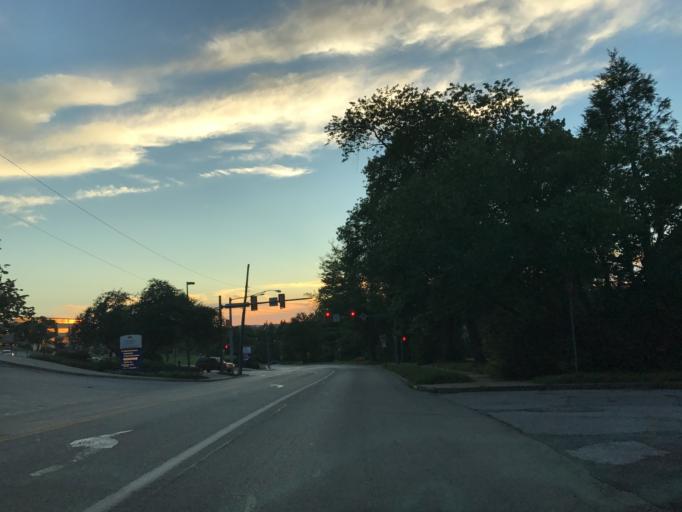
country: US
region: Pennsylvania
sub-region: York County
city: Grantley
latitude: 39.9474
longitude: -76.7165
